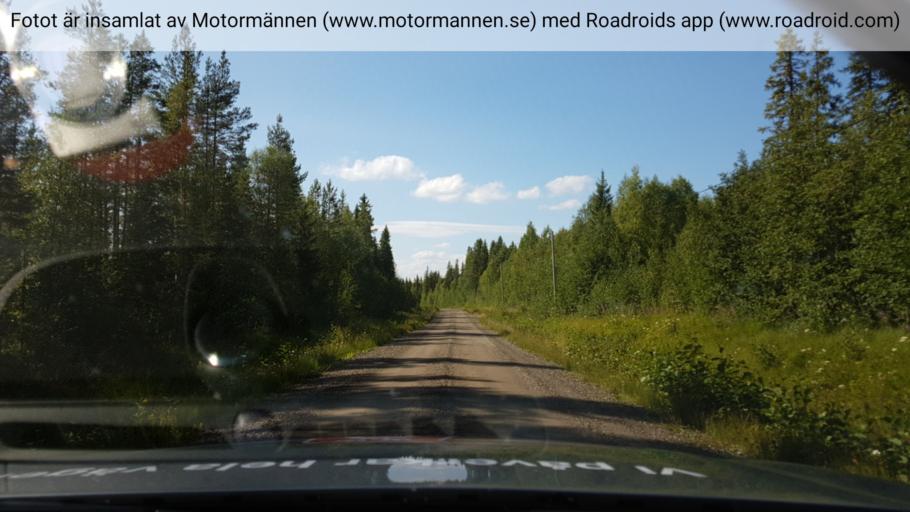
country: SE
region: Vaesterbotten
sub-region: Dorotea Kommun
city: Dorotea
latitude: 64.0948
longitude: 16.4510
